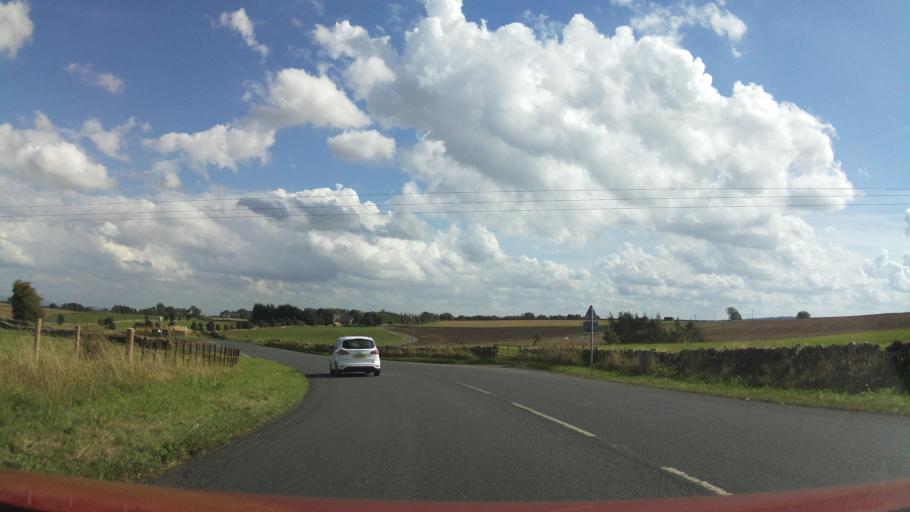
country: GB
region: England
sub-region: North Yorkshire
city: Leyburn
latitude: 54.3247
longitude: -1.8242
